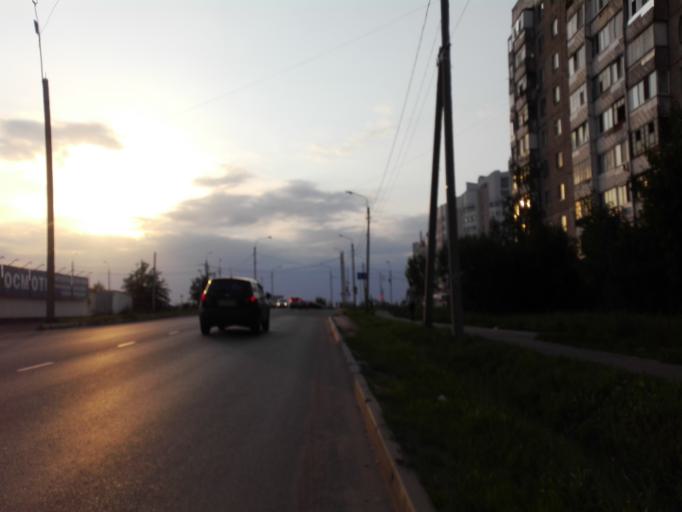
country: RU
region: Orjol
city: Orel
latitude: 53.0097
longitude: 36.1270
